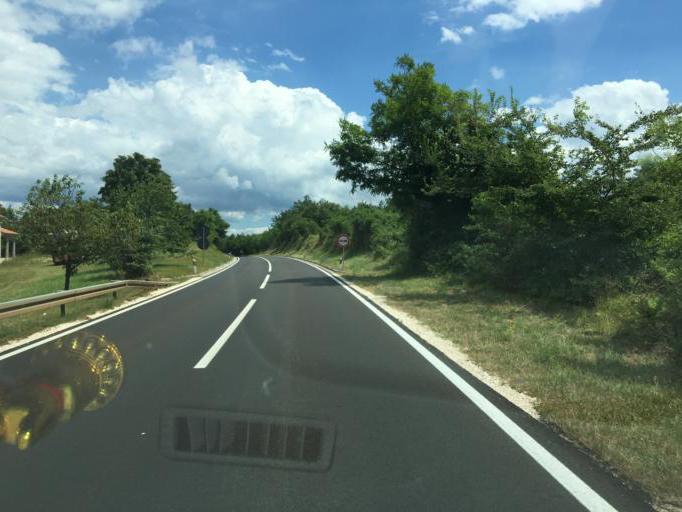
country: HR
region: Istarska
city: Karojba
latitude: 45.2449
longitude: 13.8632
